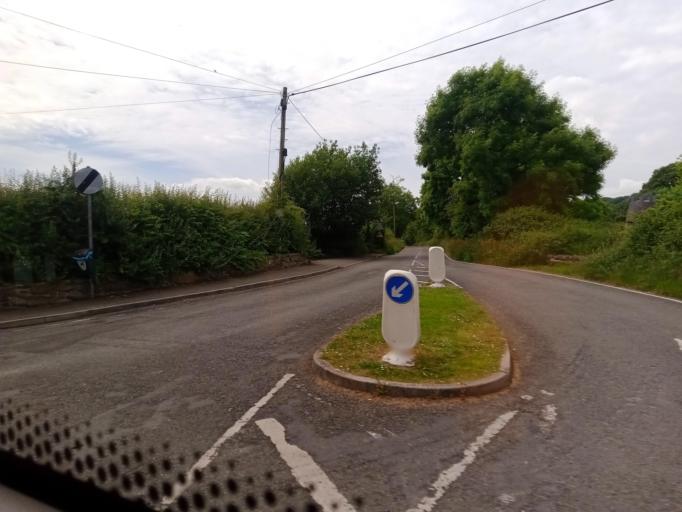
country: GB
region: Wales
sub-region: Anglesey
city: Llangoed
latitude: 53.2773
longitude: -4.0916
